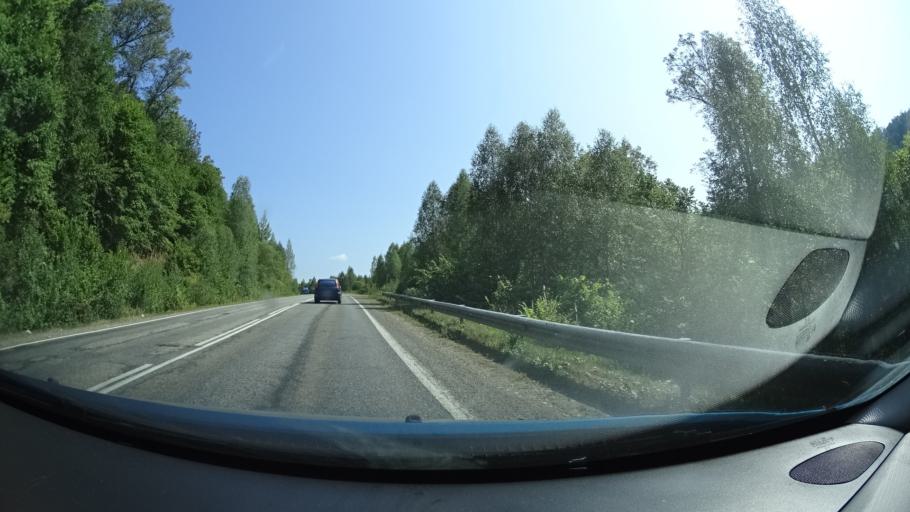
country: RU
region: Bashkortostan
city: Inzer
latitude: 54.3376
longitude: 57.1009
